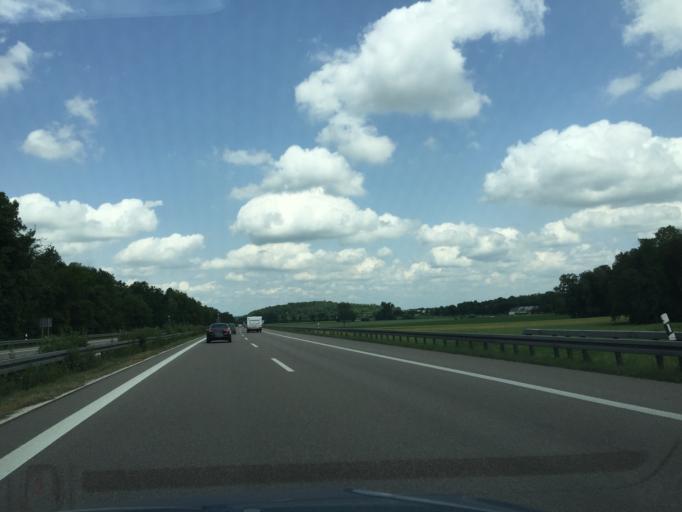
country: DE
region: Bavaria
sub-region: Swabia
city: Holzheim
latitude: 48.3924
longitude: 10.0876
